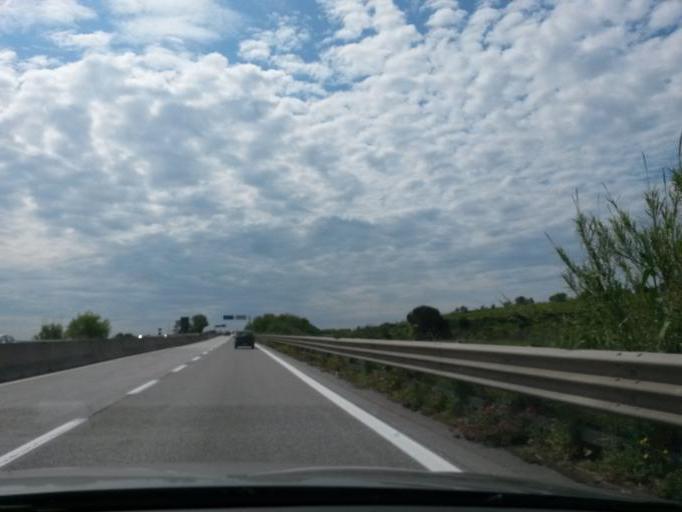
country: IT
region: Tuscany
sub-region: Provincia di Livorno
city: Cecina
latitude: 43.3210
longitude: 10.5321
